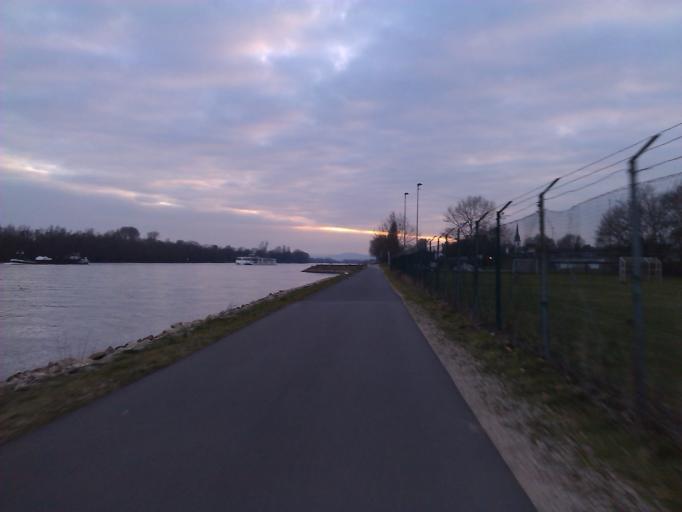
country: DE
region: Hesse
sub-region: Regierungsbezirk Darmstadt
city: Eltville
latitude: 50.0206
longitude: 8.1067
